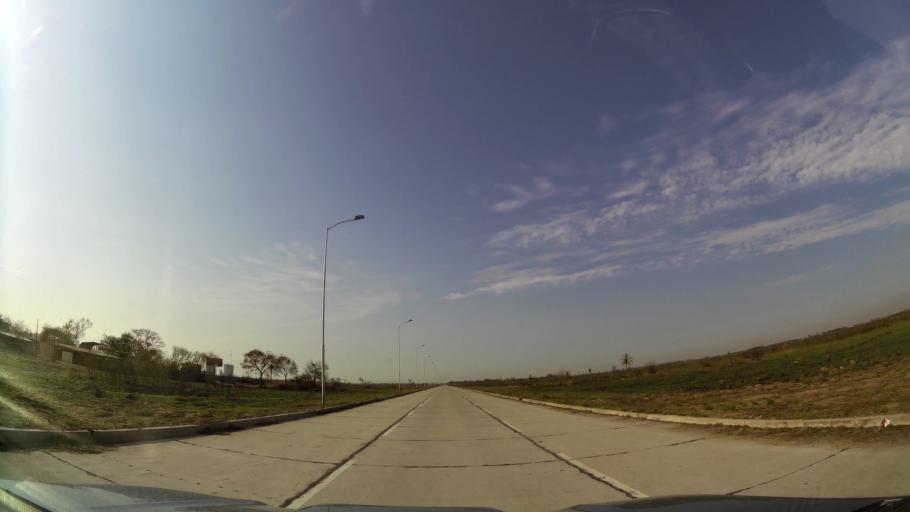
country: BO
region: Santa Cruz
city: La Belgica
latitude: -17.6543
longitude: -63.1397
